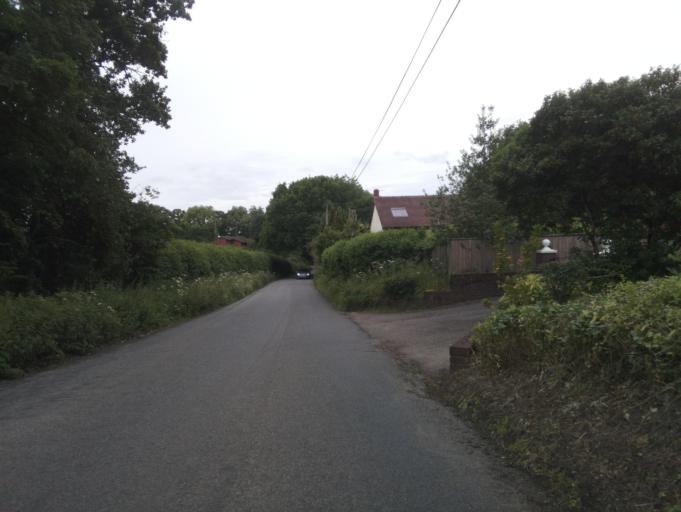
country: GB
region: England
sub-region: Devon
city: Ottery St Mary
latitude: 50.7537
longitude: -3.2544
